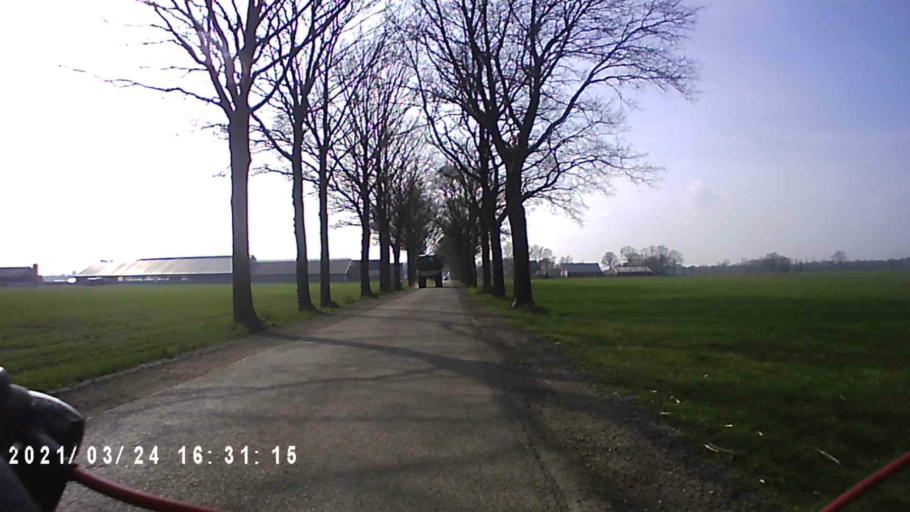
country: NL
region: Groningen
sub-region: Gemeente Leek
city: Leek
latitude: 53.0716
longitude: 6.2872
